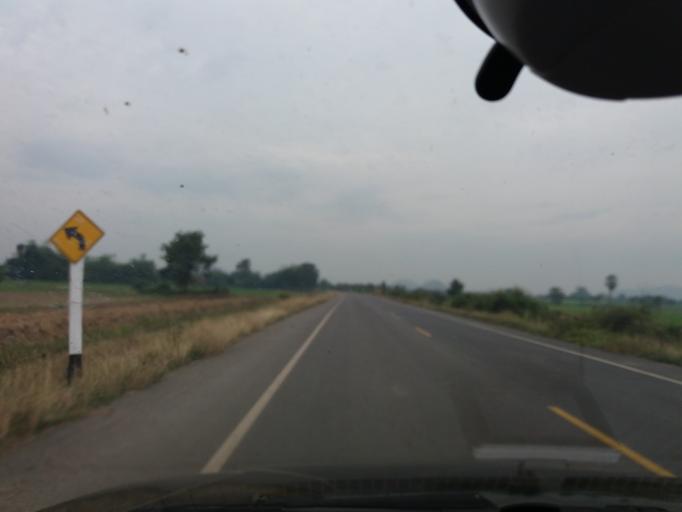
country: TH
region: Suphan Buri
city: Doem Bang Nang Buat
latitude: 14.8611
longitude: 100.1290
